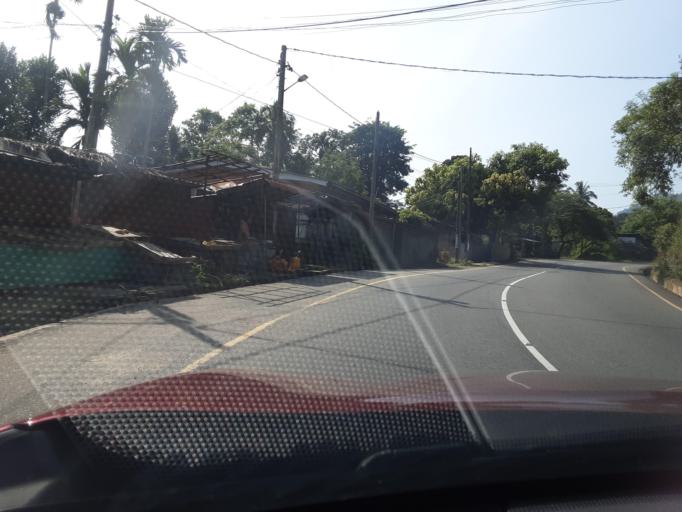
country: LK
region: Uva
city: Badulla
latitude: 6.9800
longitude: 81.0811
